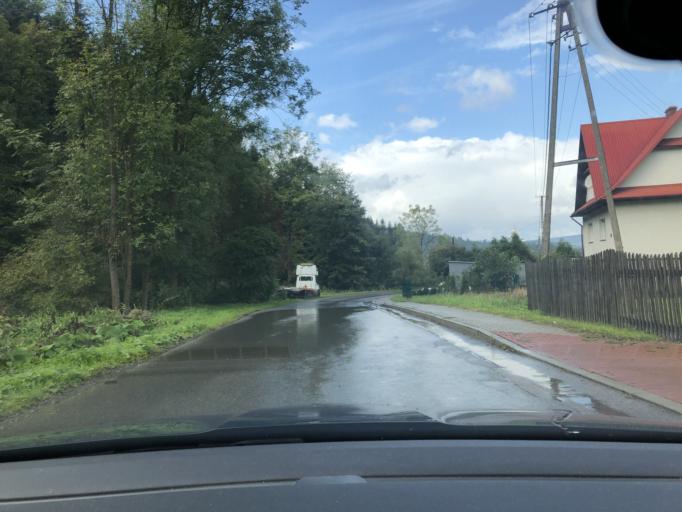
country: PL
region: Lesser Poland Voivodeship
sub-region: Powiat suski
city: Stryszawa
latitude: 49.7058
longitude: 19.5350
